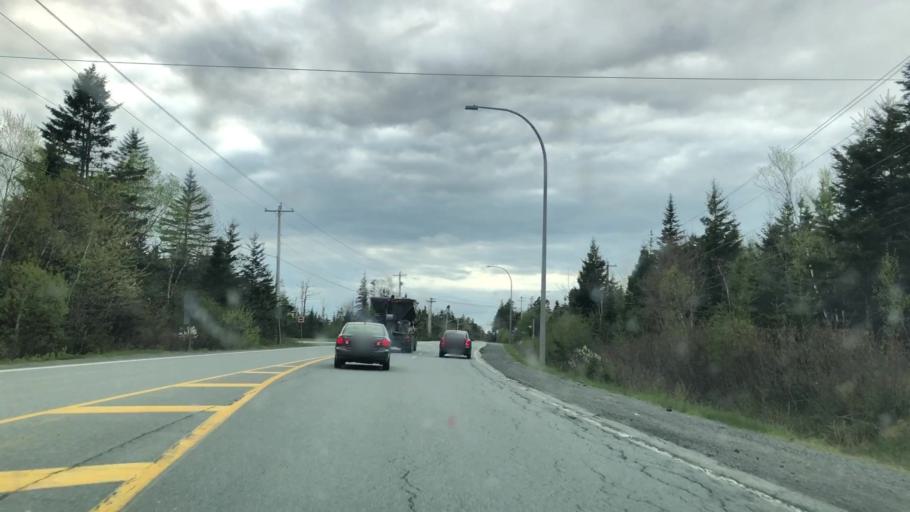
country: CA
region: Nova Scotia
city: Cole Harbour
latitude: 44.7817
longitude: -63.1761
